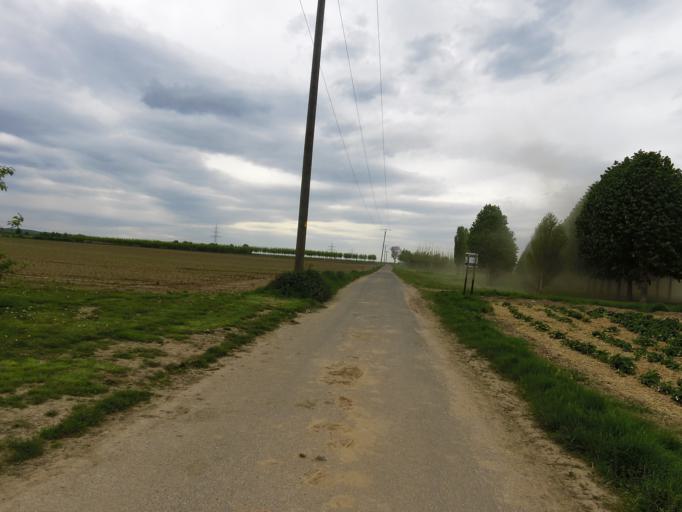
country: DE
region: North Rhine-Westphalia
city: Meckenheim
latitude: 50.6298
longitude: 7.0034
